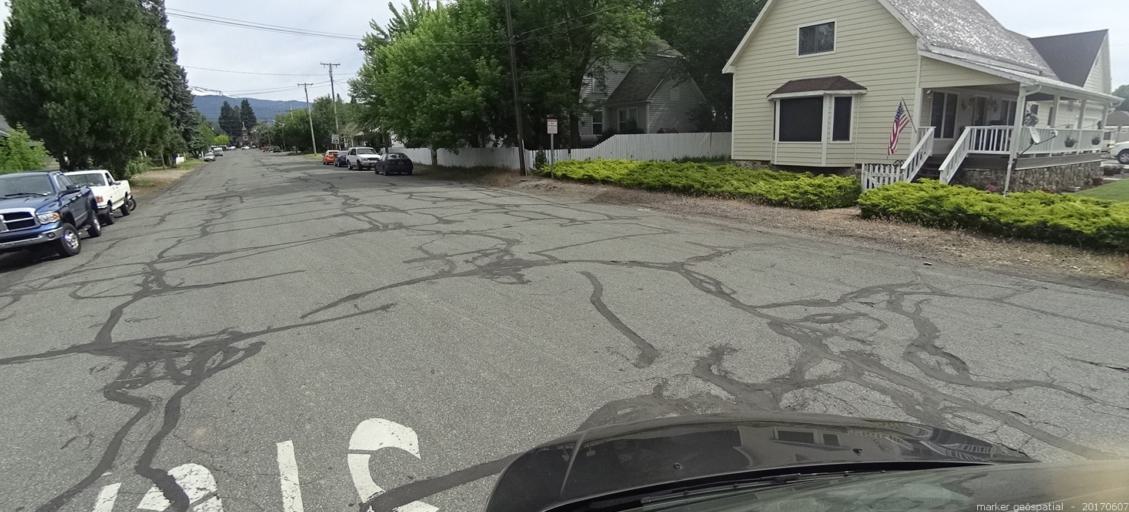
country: US
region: California
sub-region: Siskiyou County
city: McCloud
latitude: 41.2521
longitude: -122.1387
